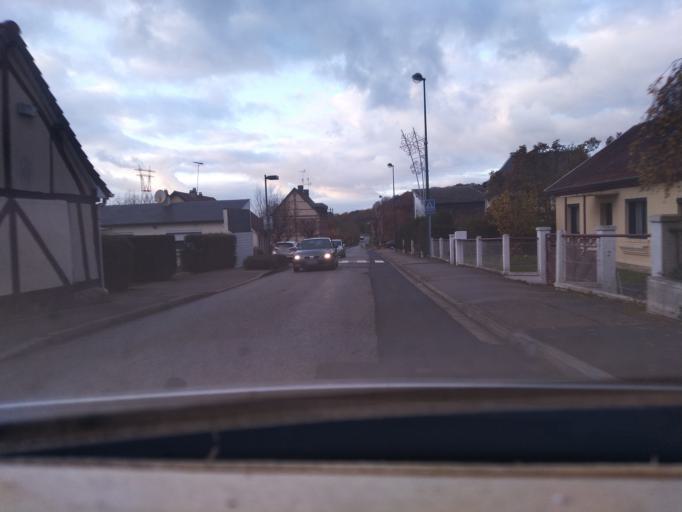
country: FR
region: Haute-Normandie
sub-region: Departement de la Seine-Maritime
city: Yainville
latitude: 49.4548
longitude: 0.8293
